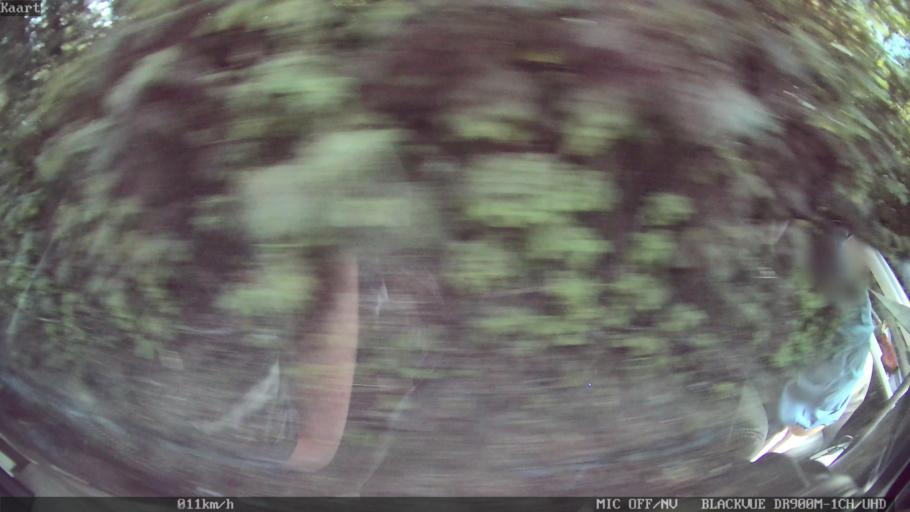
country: ID
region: Bali
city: Banjar Kedisan
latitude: -8.2801
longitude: 115.3711
